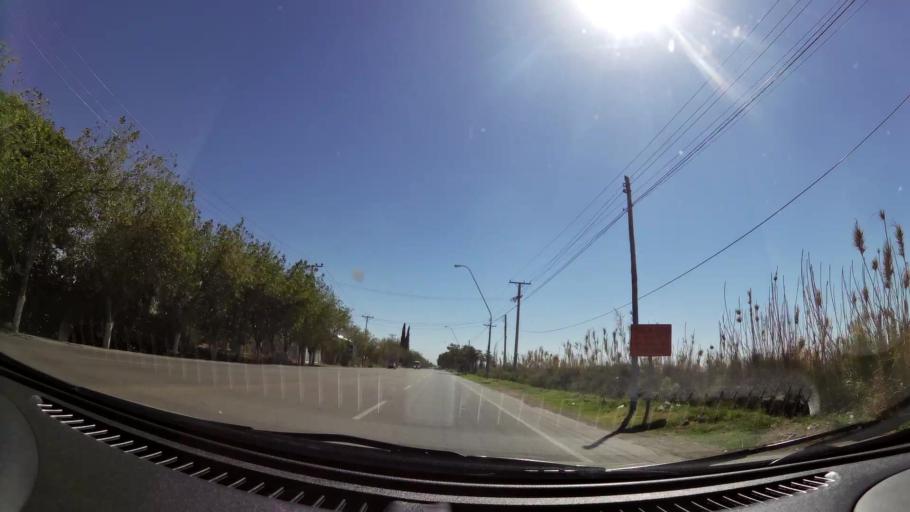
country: AR
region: San Juan
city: Villa Krause
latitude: -31.6010
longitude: -68.5421
